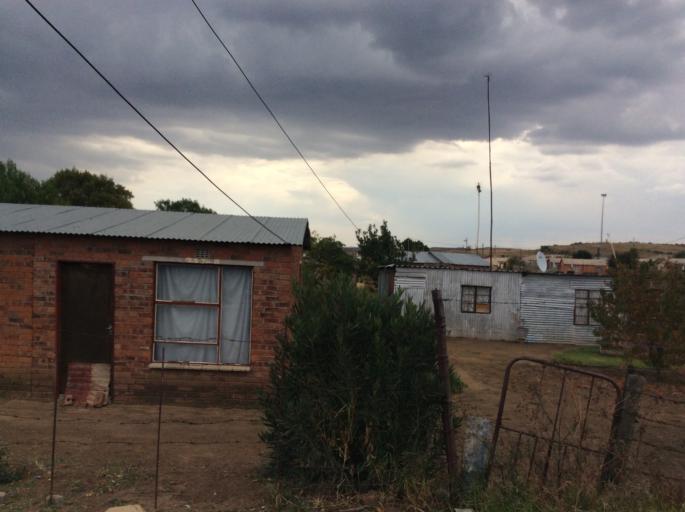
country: LS
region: Mafeteng
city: Mafeteng
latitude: -29.7189
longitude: 27.0308
